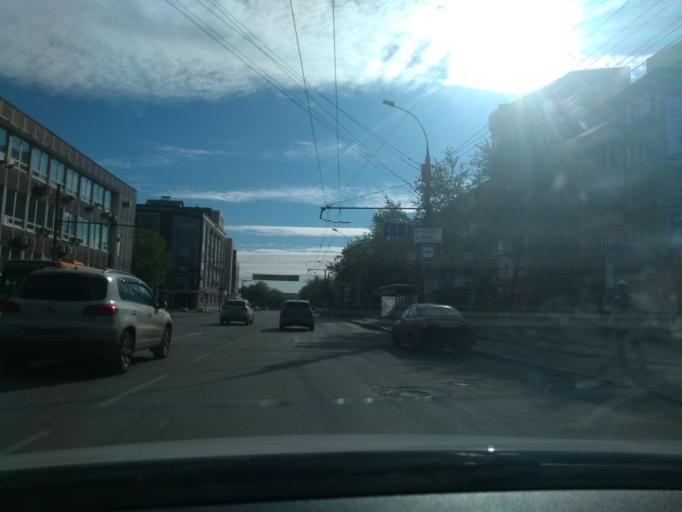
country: RU
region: Perm
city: Perm
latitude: 57.9969
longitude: 56.2640
